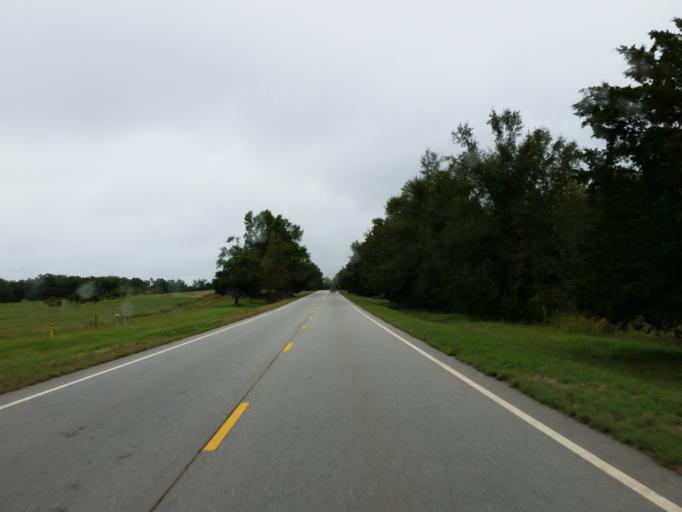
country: US
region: Georgia
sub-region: Lamar County
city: Barnesville
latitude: 32.9638
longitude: -84.1111
